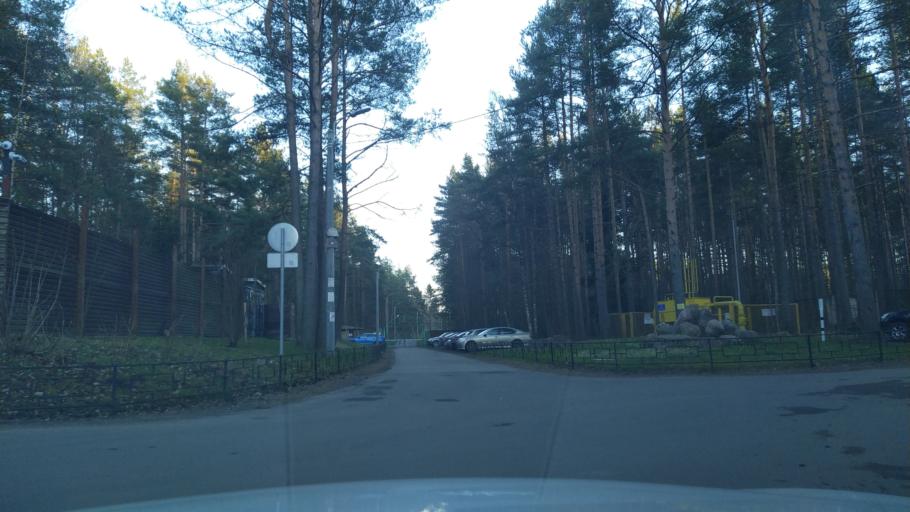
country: RU
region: St.-Petersburg
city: Solnechnoye
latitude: 60.1452
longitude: 29.9385
